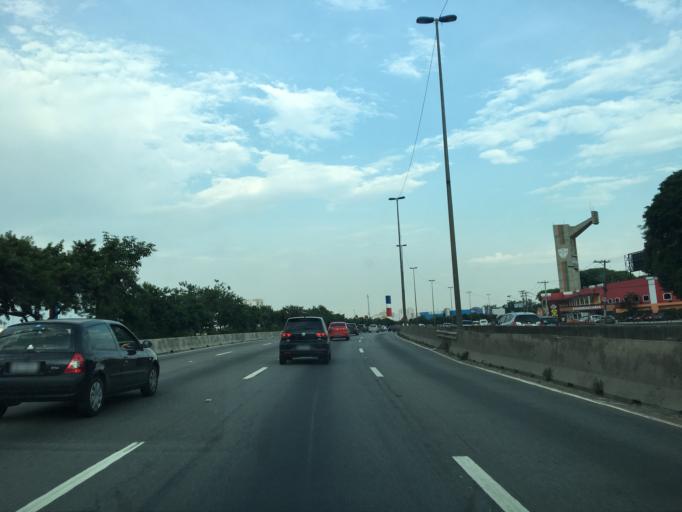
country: BR
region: Sao Paulo
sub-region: Sao Paulo
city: Sao Paulo
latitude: -23.5194
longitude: -46.6202
